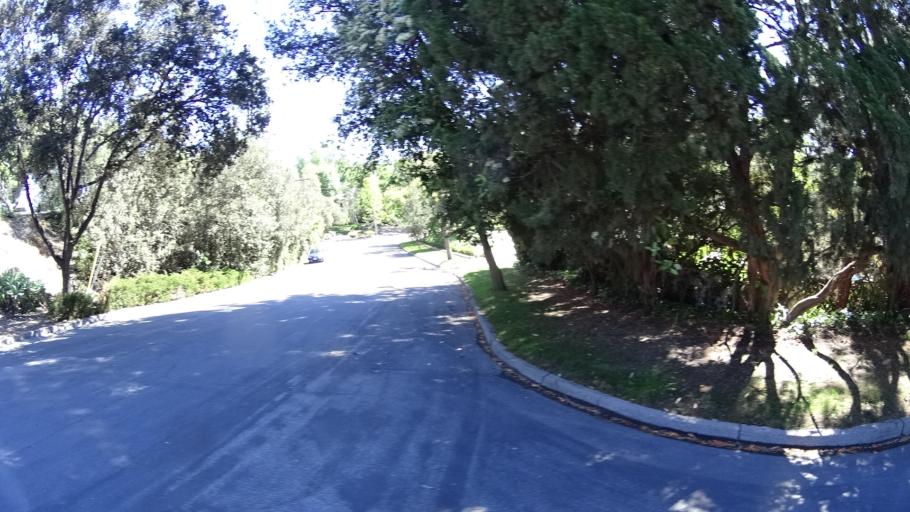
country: US
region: California
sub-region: Ventura County
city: Thousand Oaks
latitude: 34.1906
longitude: -118.8510
